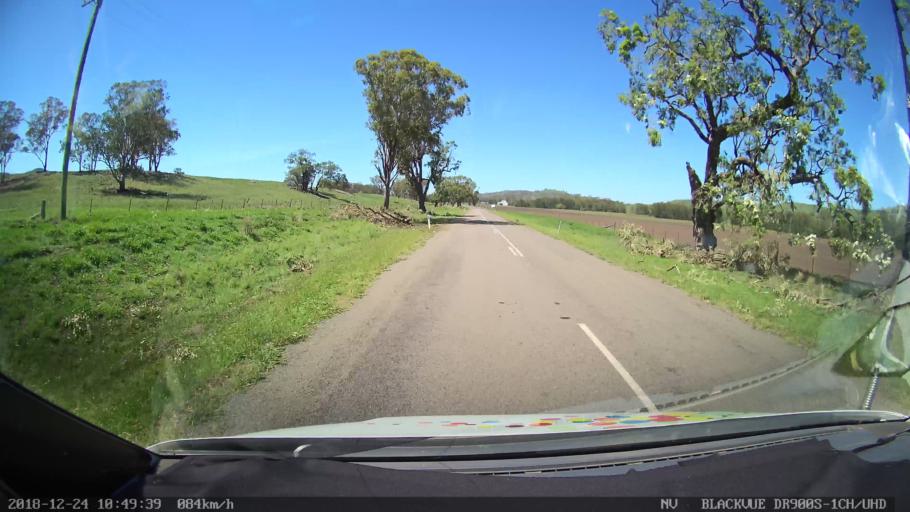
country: AU
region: New South Wales
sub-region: Upper Hunter Shire
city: Merriwa
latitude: -31.9501
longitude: 150.4264
